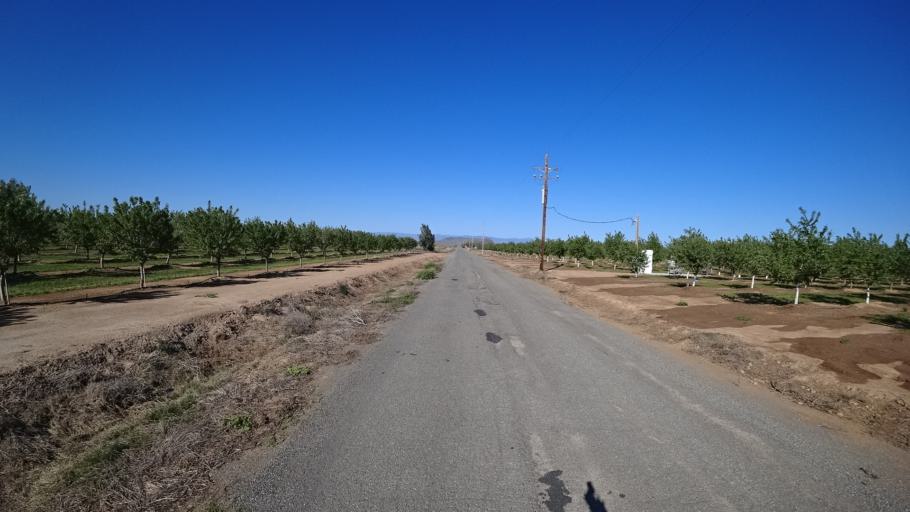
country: US
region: California
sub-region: Glenn County
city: Orland
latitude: 39.7478
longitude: -122.2426
